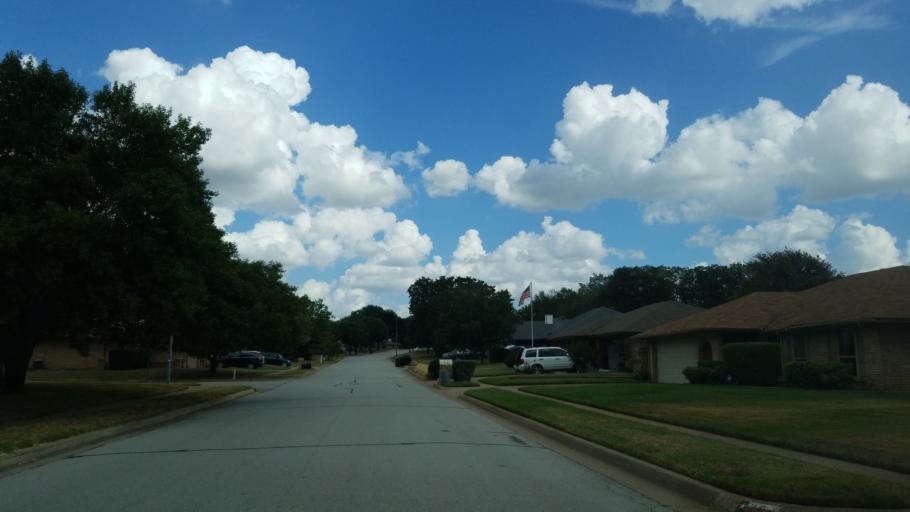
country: US
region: Texas
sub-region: Tarrant County
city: Euless
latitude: 32.8740
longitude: -97.0792
